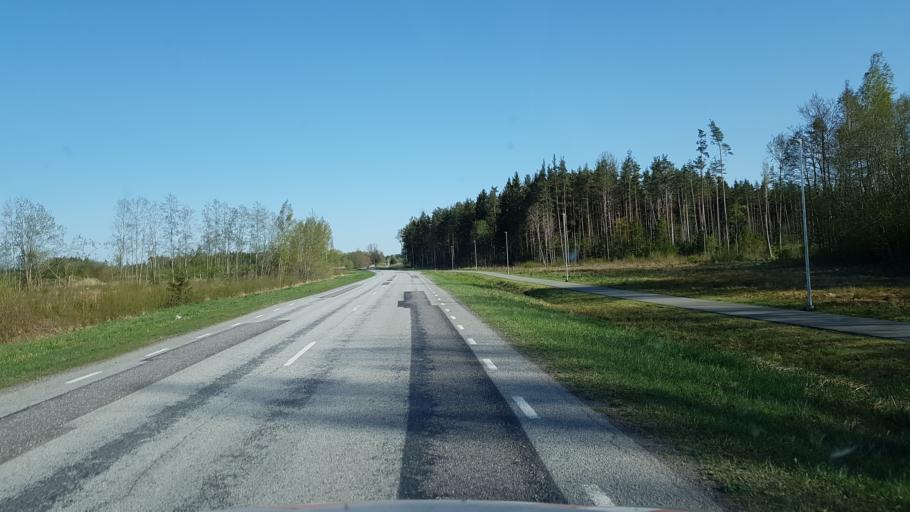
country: EE
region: Paernumaa
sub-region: Paikuse vald
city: Paikuse
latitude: 58.3675
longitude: 24.6387
